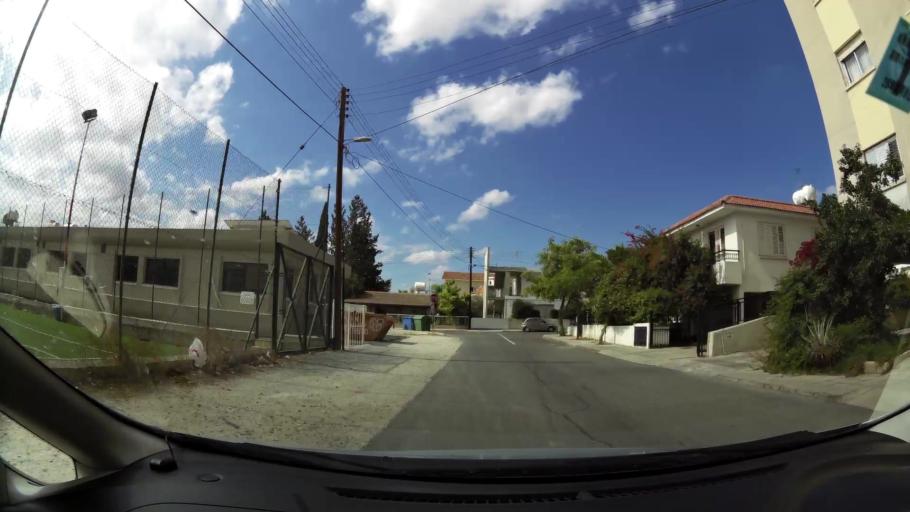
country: CY
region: Lefkosia
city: Nicosia
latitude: 35.1494
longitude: 33.3658
